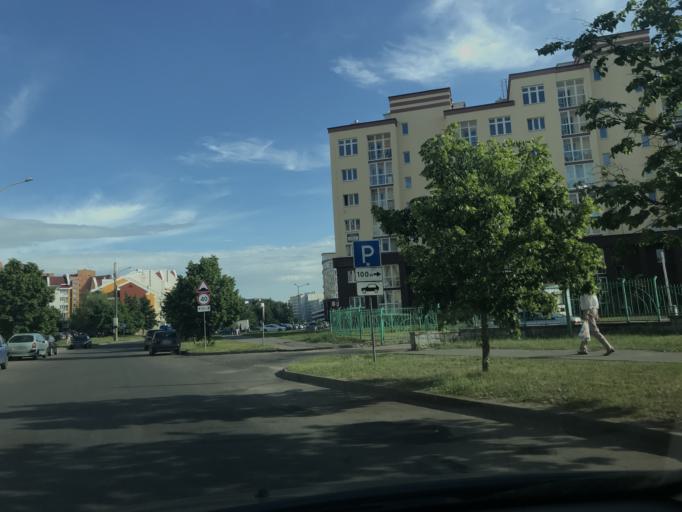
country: BY
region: Minsk
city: Borovlyany
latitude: 53.9512
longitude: 27.6831
